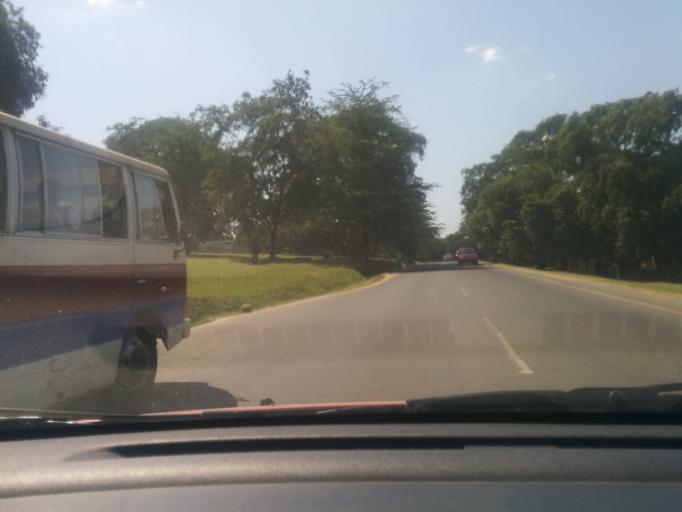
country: TZ
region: Dar es Salaam
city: Magomeni
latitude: -6.7764
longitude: 39.2085
